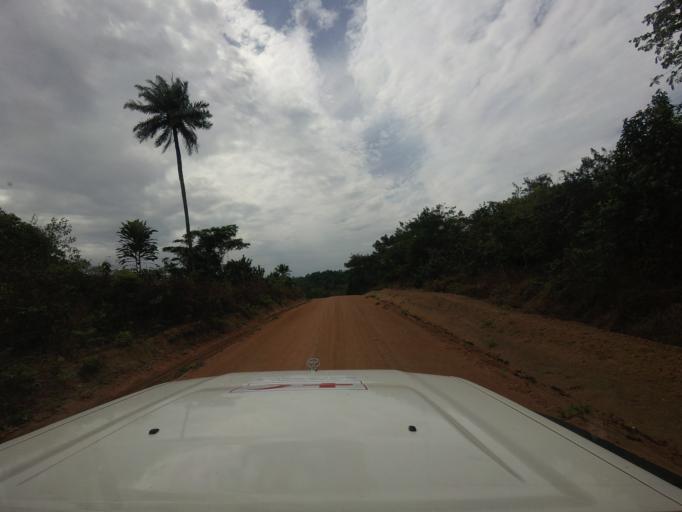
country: SL
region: Eastern Province
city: Buedu
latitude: 8.2414
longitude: -10.2222
